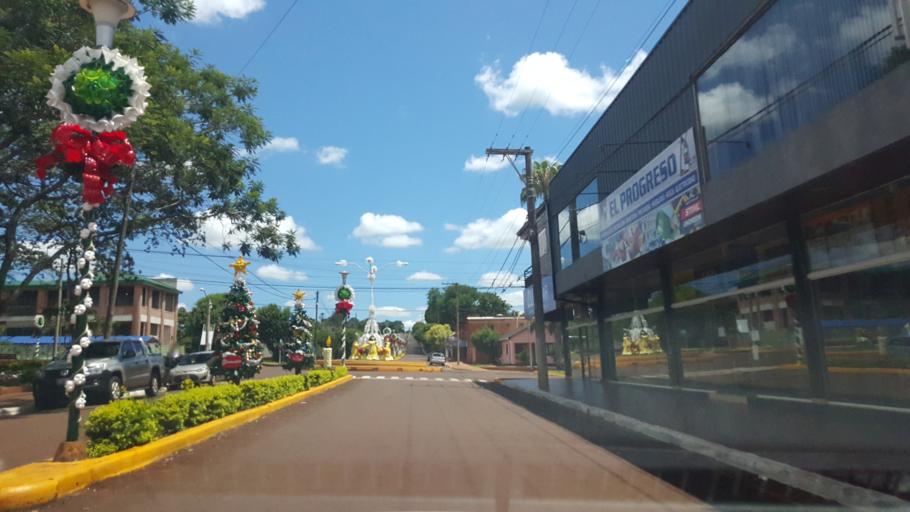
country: AR
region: Misiones
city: Capiovi
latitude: -26.9288
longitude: -55.0578
